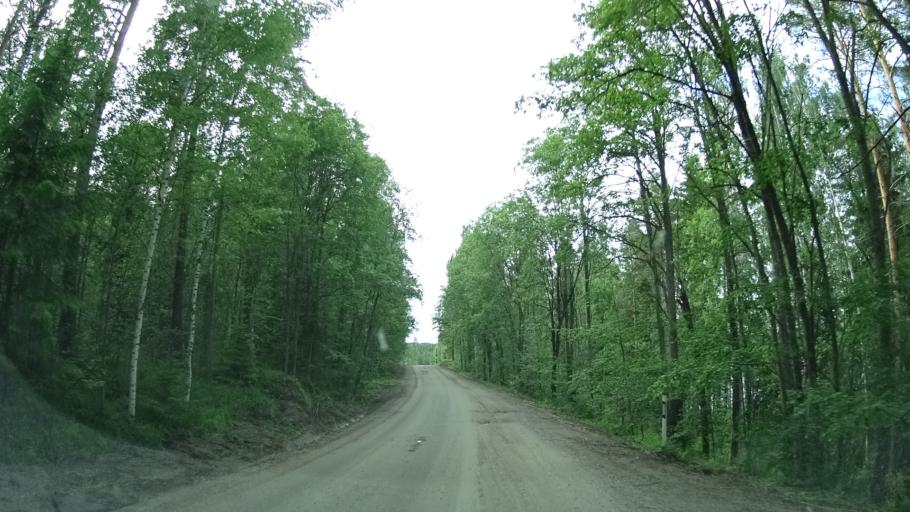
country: FI
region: Central Finland
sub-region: Joutsa
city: Luhanka
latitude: 61.6835
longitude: 25.6850
